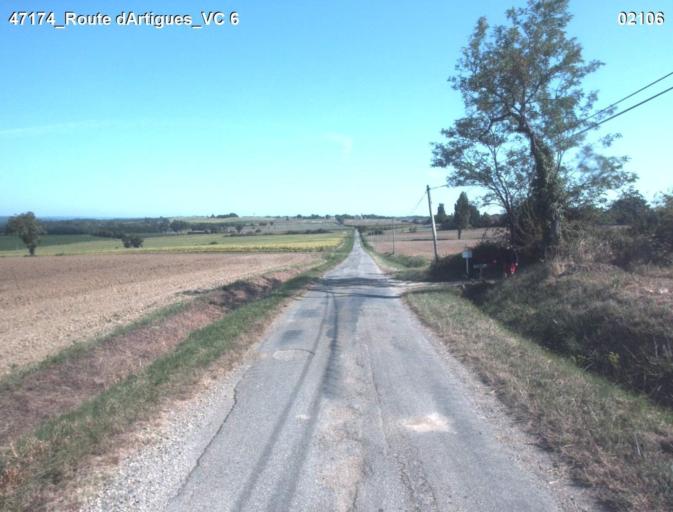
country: FR
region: Midi-Pyrenees
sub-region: Departement du Gers
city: Condom
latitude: 44.0256
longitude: 0.3331
